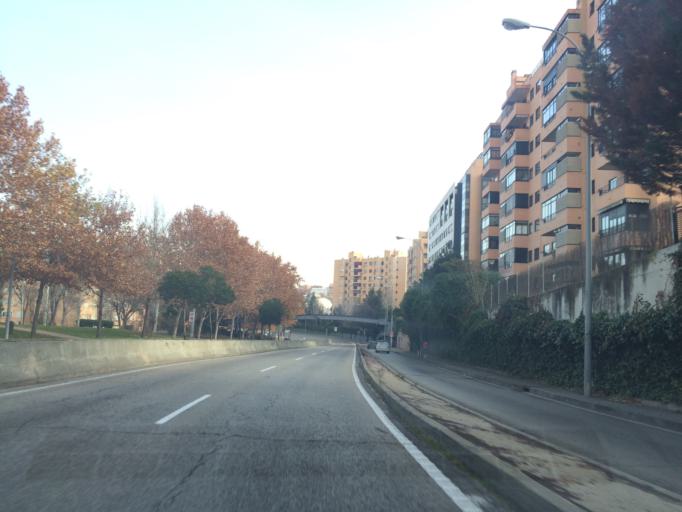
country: ES
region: Madrid
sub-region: Provincia de Madrid
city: Tetuan de las Victorias
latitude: 40.4661
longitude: -3.7176
